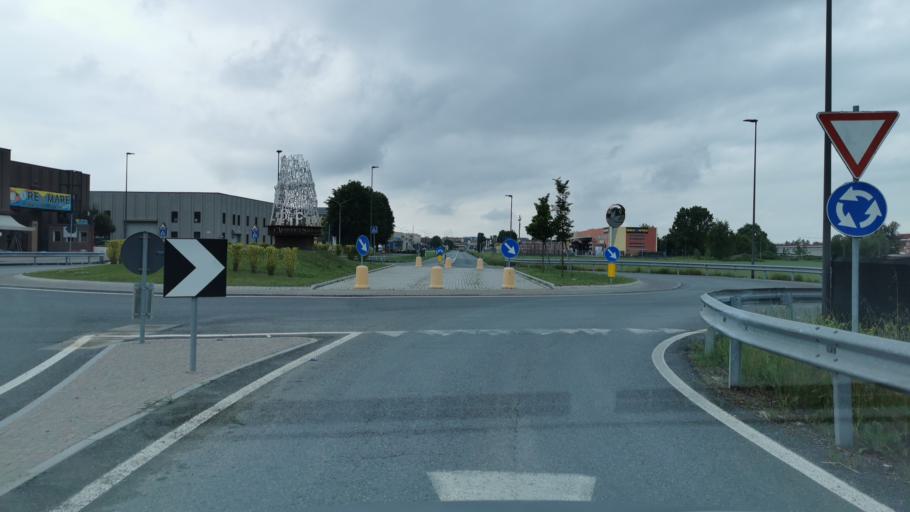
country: IT
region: Piedmont
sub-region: Provincia di Cuneo
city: Savigliano
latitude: 44.6600
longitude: 7.6564
